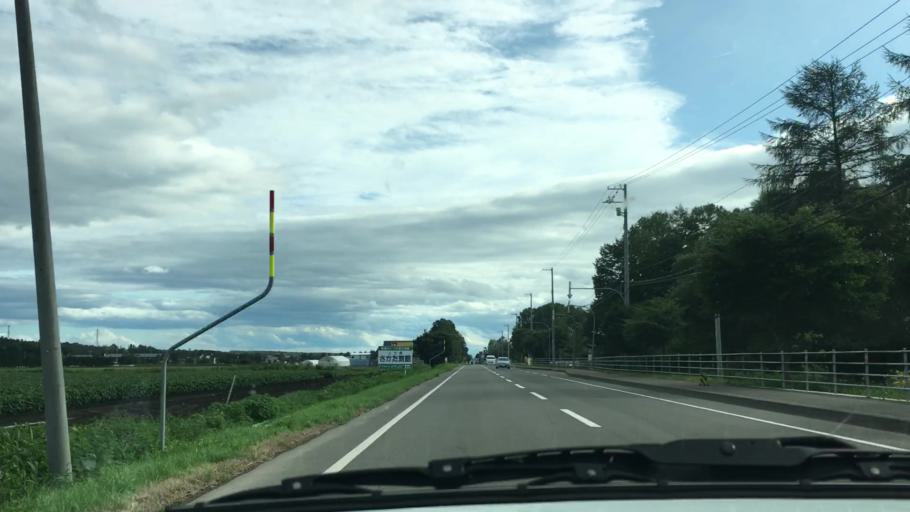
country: JP
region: Hokkaido
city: Otofuke
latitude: 43.2460
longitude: 143.2981
